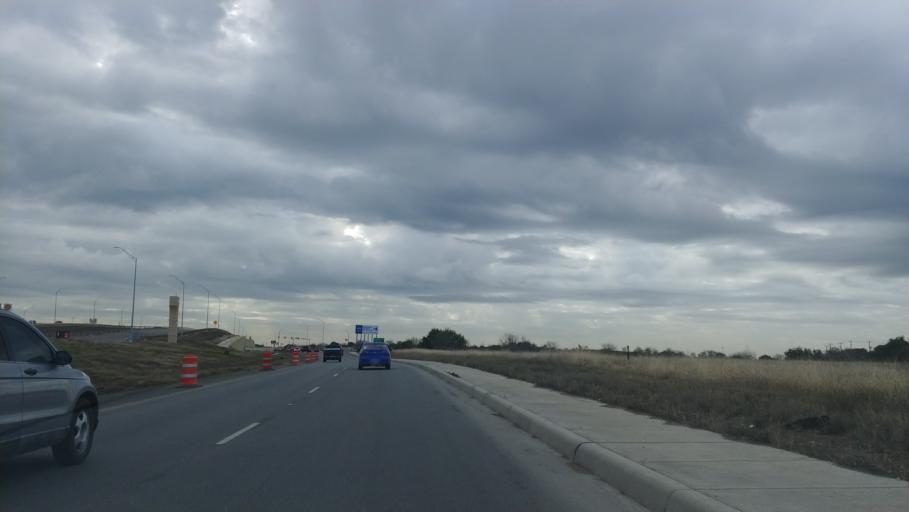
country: US
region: Texas
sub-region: Bexar County
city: Lackland Air Force Base
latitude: 29.4064
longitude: -98.7095
